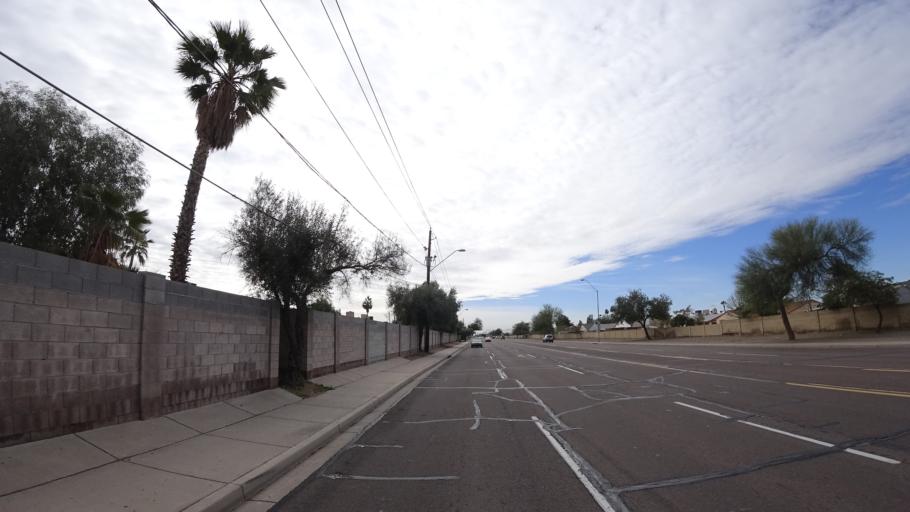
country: US
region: Arizona
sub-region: Maricopa County
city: Glendale
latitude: 33.6024
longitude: -112.1685
